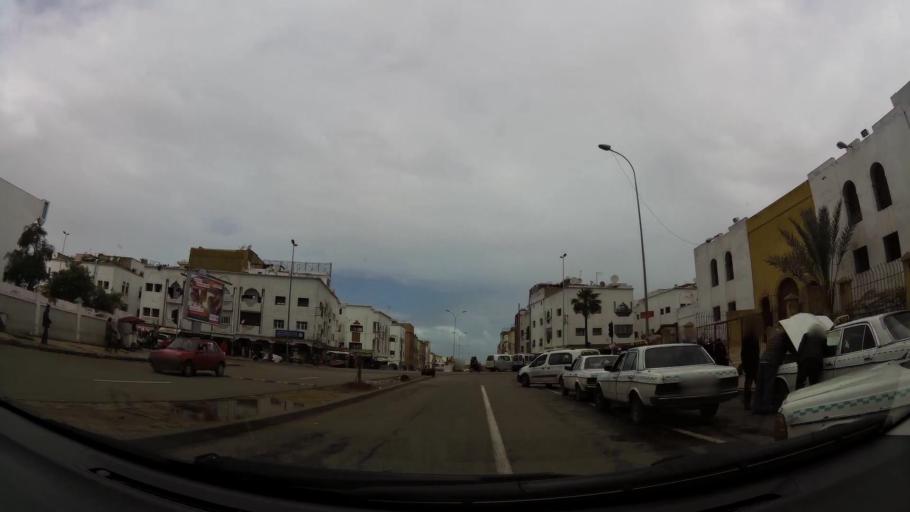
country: MA
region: Grand Casablanca
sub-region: Casablanca
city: Casablanca
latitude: 33.5545
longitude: -7.6860
